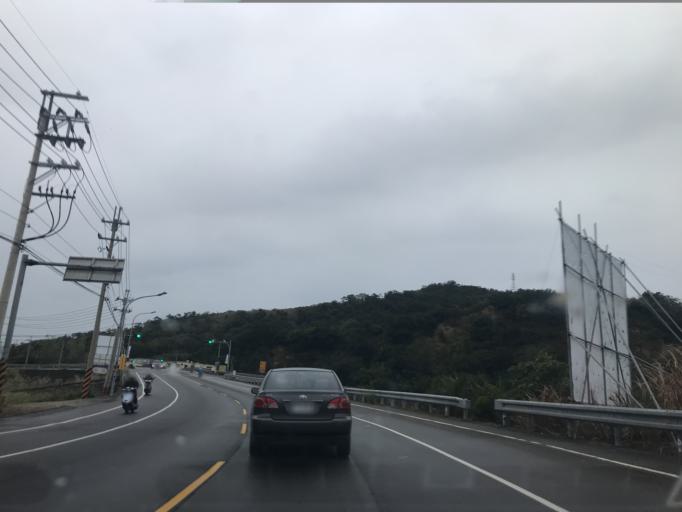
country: TW
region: Taiwan
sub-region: Hsinchu
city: Zhubei
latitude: 24.8392
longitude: 121.1000
